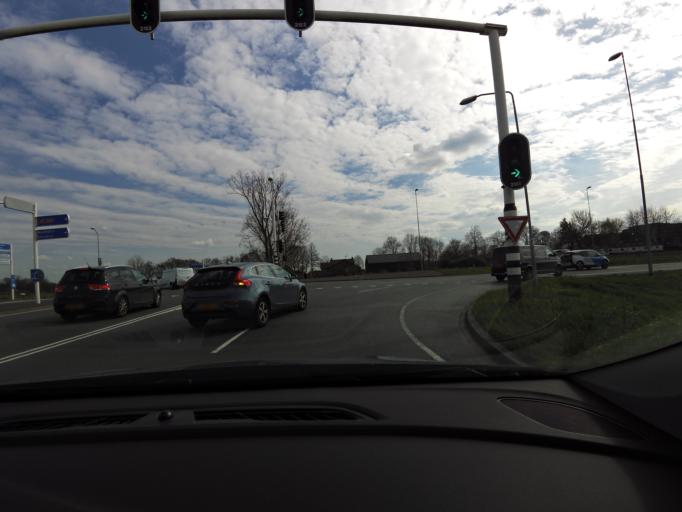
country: NL
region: North Brabant
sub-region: Gemeente 's-Hertogenbosch
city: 's-Hertogenbosch
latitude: 51.7164
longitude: 5.3421
